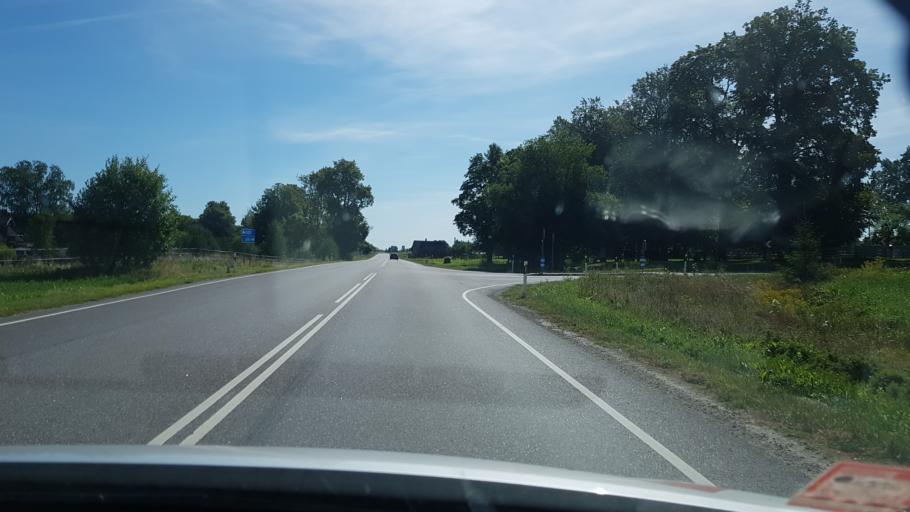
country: EE
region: Tartu
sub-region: Tartu linn
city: Tartu
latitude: 58.4349
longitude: 26.8334
